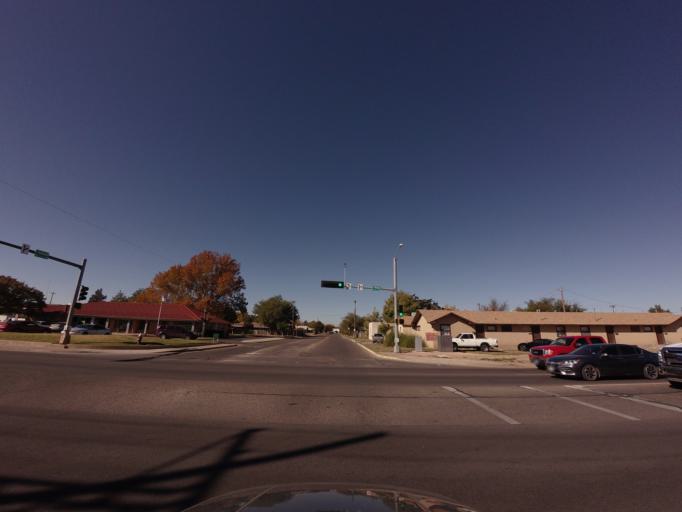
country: US
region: New Mexico
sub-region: Curry County
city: Clovis
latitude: 34.4267
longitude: -103.1964
